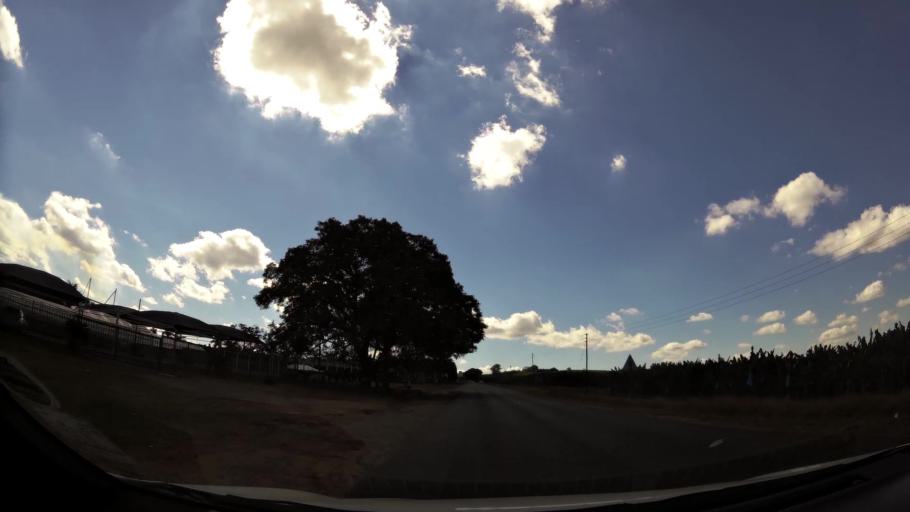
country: ZA
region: Limpopo
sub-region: Mopani District Municipality
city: Tzaneen
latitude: -23.8123
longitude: 30.1733
